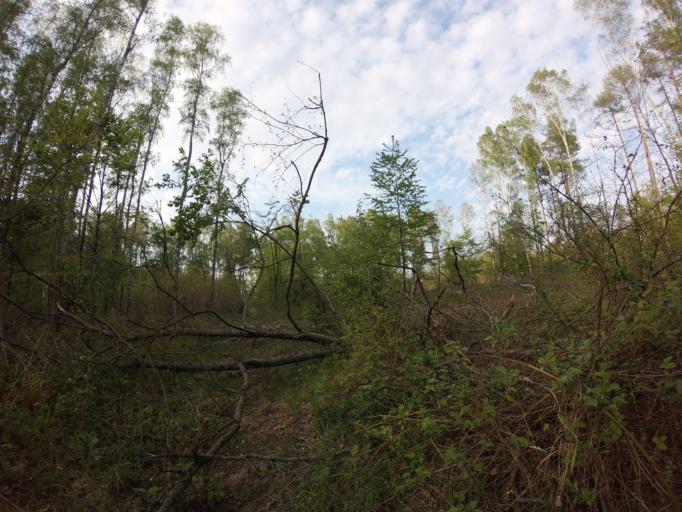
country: PL
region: West Pomeranian Voivodeship
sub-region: Powiat choszczenski
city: Choszczno
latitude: 53.1493
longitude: 15.3416
